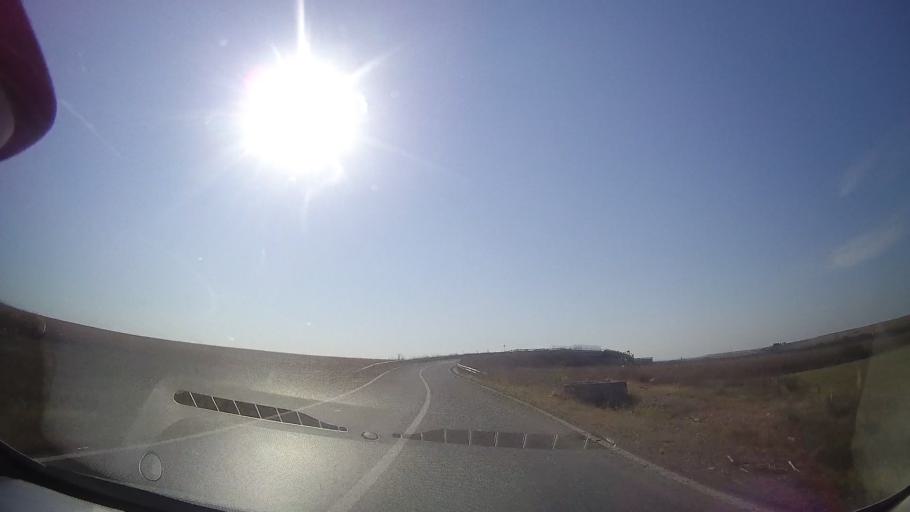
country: RO
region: Timis
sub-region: Comuna Topolovatu Mare
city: Topolovatu Mare
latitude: 45.8077
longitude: 21.5842
